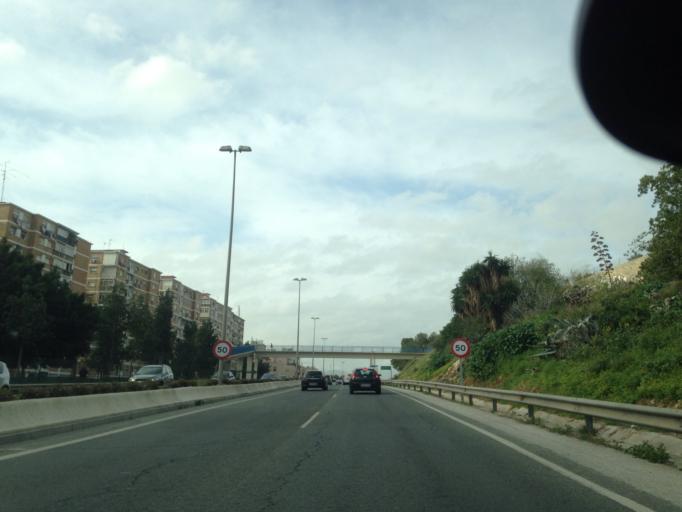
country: ES
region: Andalusia
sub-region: Provincia de Malaga
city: Malaga
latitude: 36.7316
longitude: -4.4417
